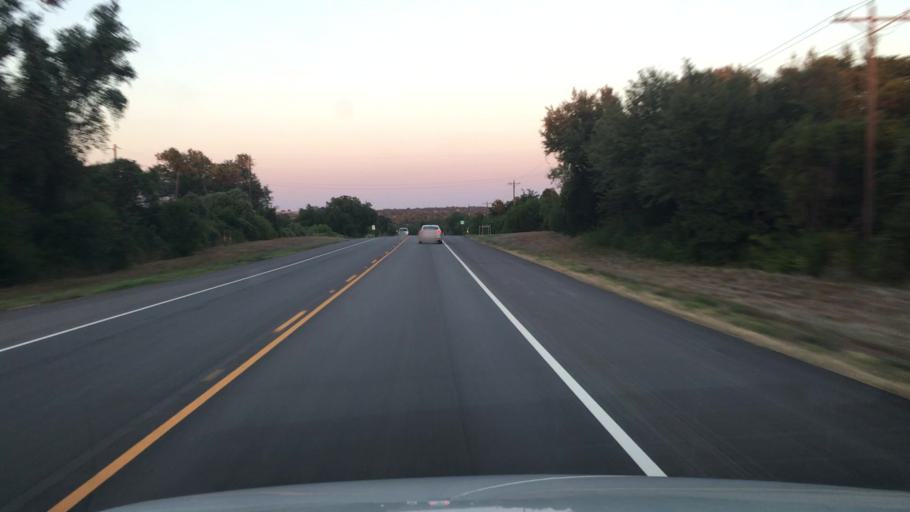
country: US
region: Texas
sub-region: Somervell County
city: Glen Rose
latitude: 32.1914
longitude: -97.8336
